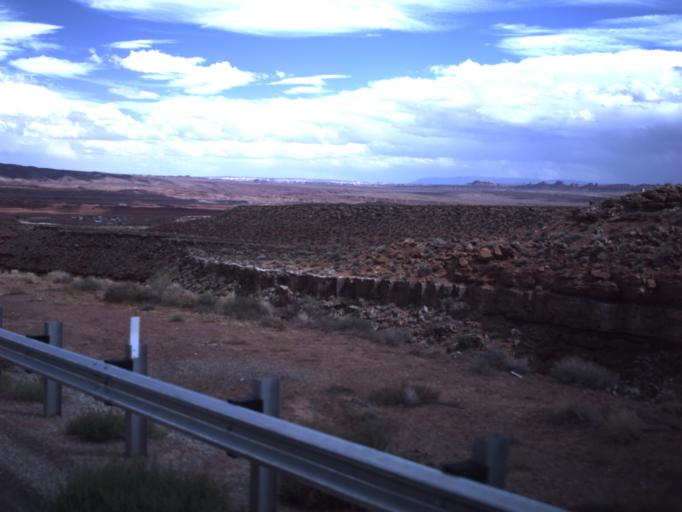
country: US
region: Arizona
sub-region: Navajo County
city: Kayenta
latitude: 37.1268
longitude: -109.9223
